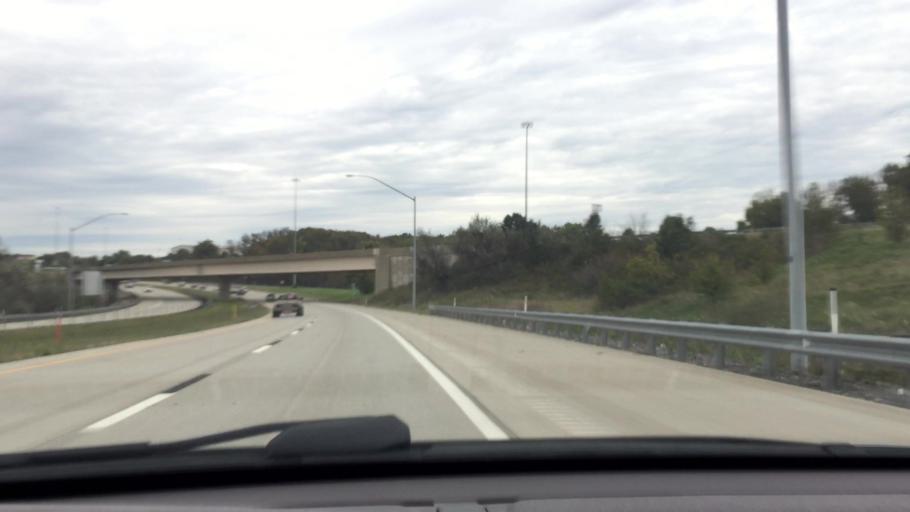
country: US
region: Pennsylvania
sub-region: Allegheny County
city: Carnot-Moon
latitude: 40.5209
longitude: -80.2741
